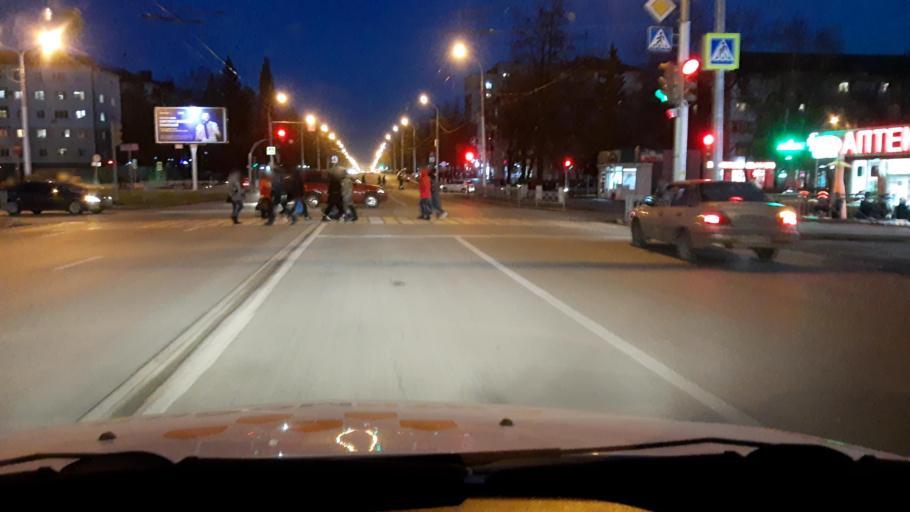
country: RU
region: Bashkortostan
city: Ufa
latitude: 54.8106
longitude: 56.0995
